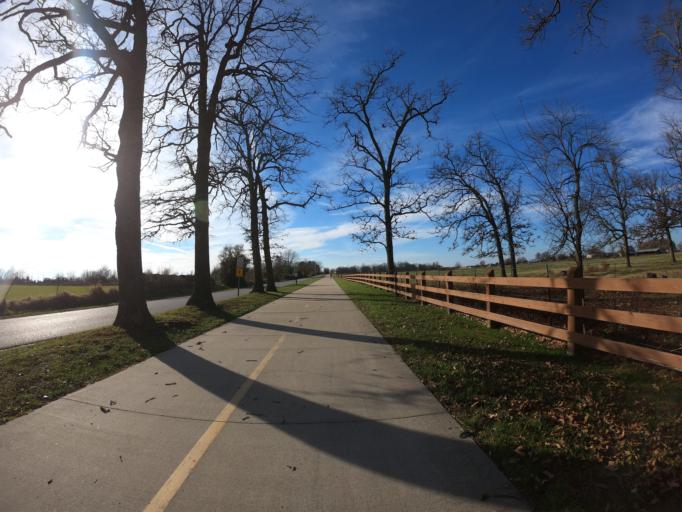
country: US
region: Arkansas
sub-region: Benton County
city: Lowell
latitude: 36.2655
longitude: -94.1550
